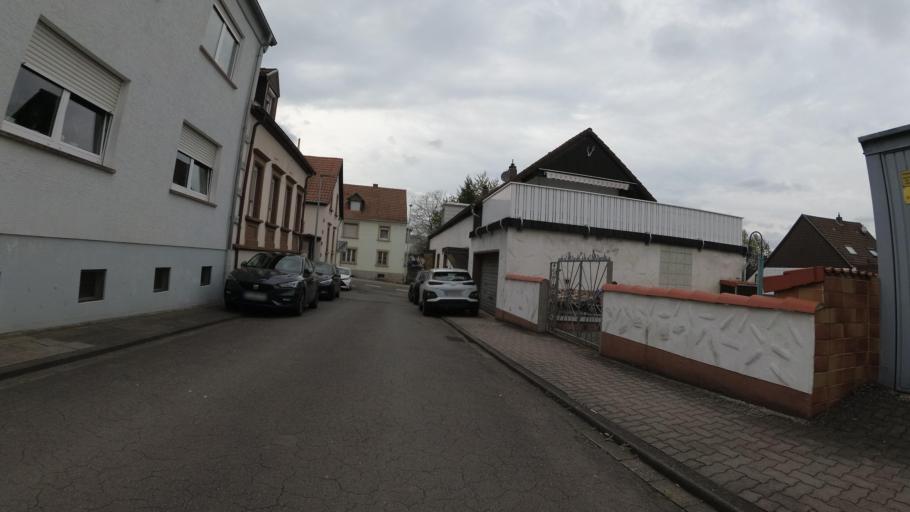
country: DE
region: Rheinland-Pfalz
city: Zweibrucken
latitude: 49.2445
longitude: 7.3501
